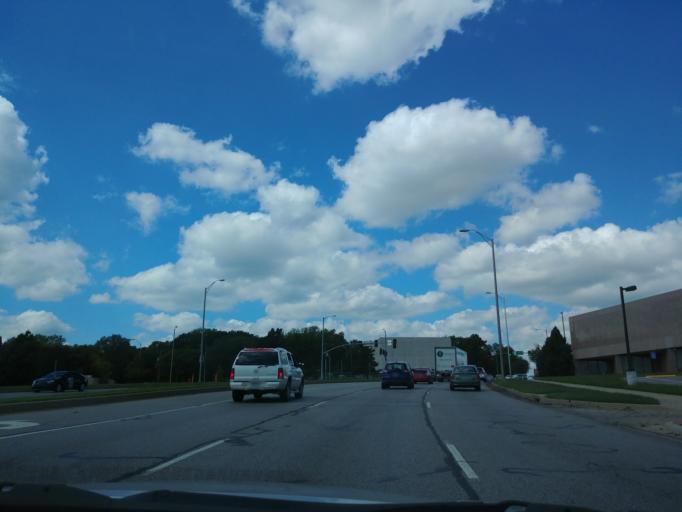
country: US
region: Missouri
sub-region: Jackson County
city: Kansas City
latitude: 39.0362
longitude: -94.5418
